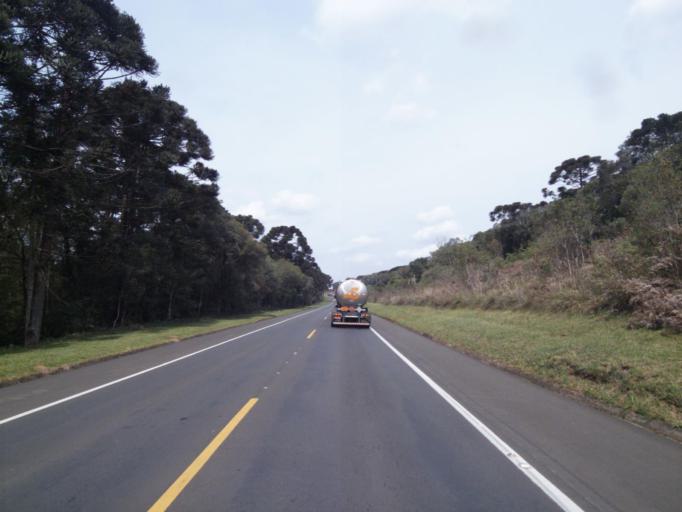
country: BR
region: Parana
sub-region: Irati
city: Irati
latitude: -25.4617
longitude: -50.4242
